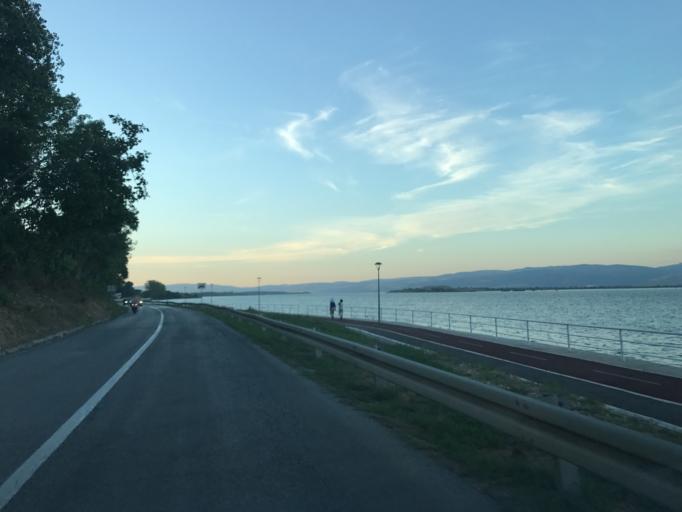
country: RS
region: Central Serbia
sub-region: Branicevski Okrug
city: Golubac
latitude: 44.6593
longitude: 21.6164
